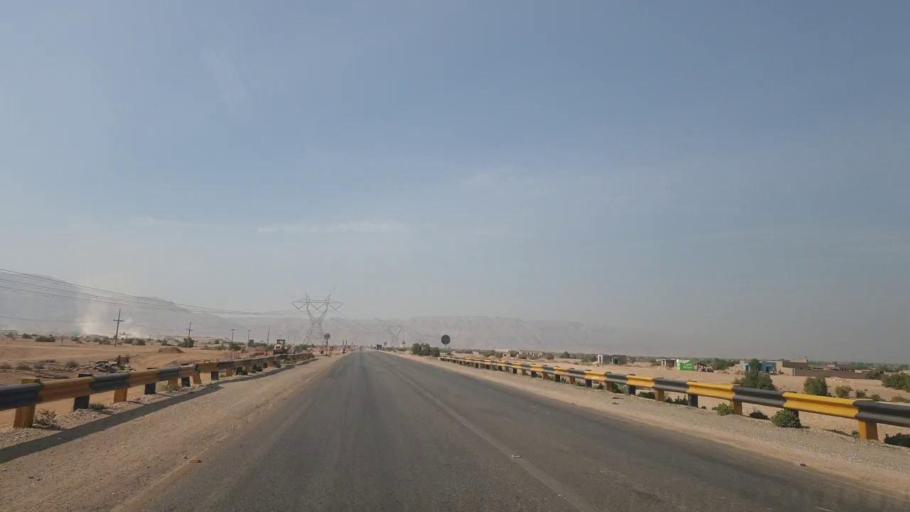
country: PK
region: Sindh
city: Sehwan
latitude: 26.2071
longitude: 67.9287
